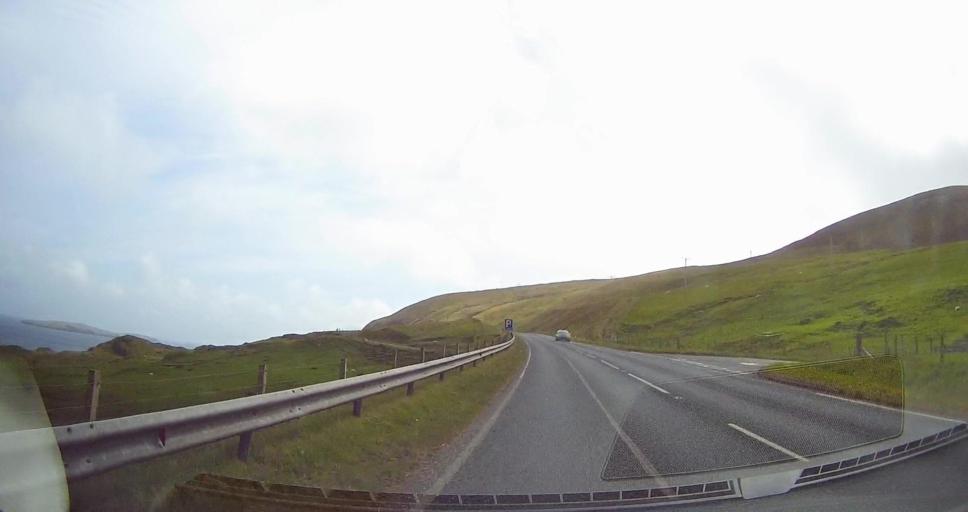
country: GB
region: Scotland
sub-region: Shetland Islands
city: Sandwick
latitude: 60.0261
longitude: -1.2366
